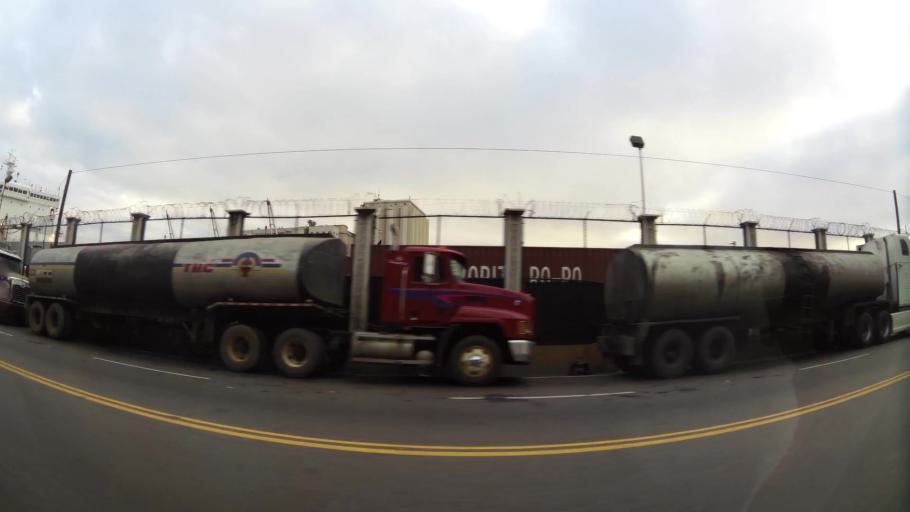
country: DO
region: Nacional
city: Ciudad Nueva
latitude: 18.4738
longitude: -69.8817
